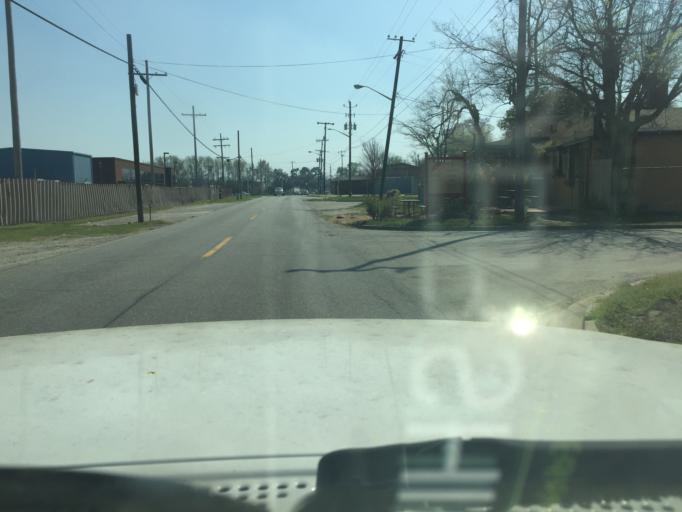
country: US
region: Georgia
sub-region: Chatham County
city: Savannah
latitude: 32.0885
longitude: -81.1113
